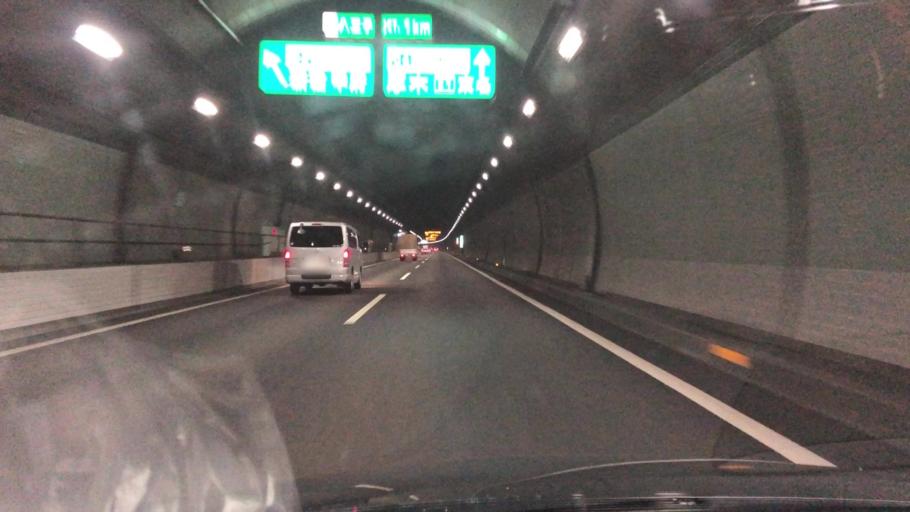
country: JP
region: Tokyo
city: Hachioji
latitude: 35.6535
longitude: 139.2497
